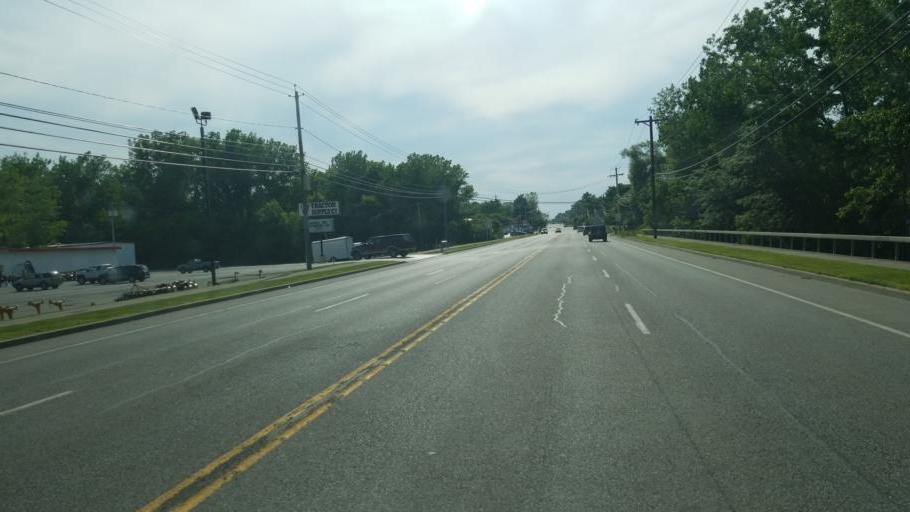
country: US
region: New York
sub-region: Genesee County
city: Batavia
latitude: 42.9931
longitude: -78.1518
